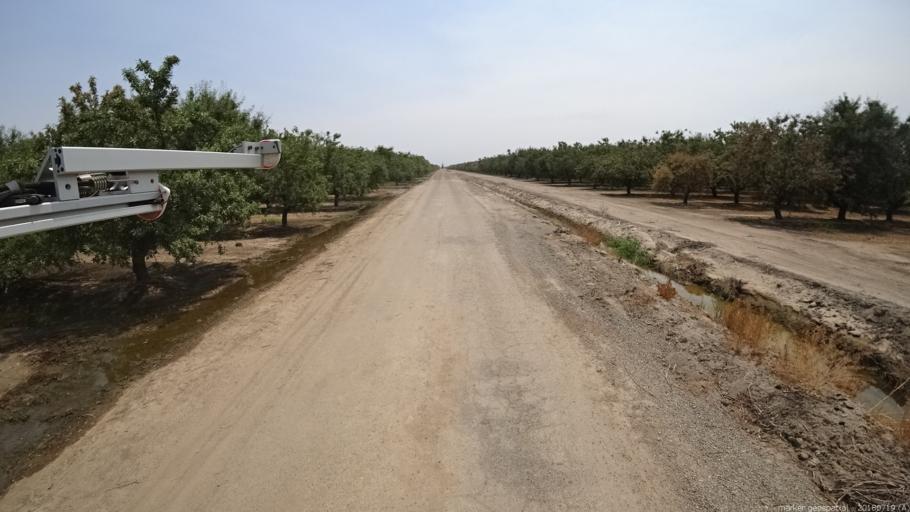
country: US
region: California
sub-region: Madera County
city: Fairmead
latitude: 37.0910
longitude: -120.1468
